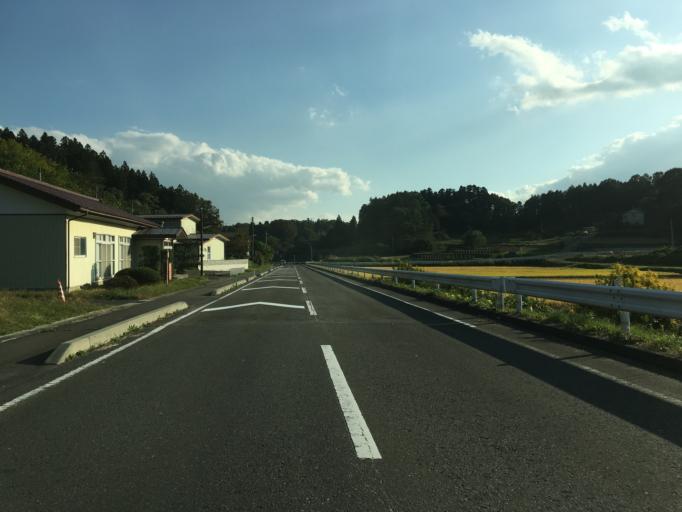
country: JP
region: Fukushima
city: Fukushima-shi
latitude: 37.6670
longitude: 140.5398
